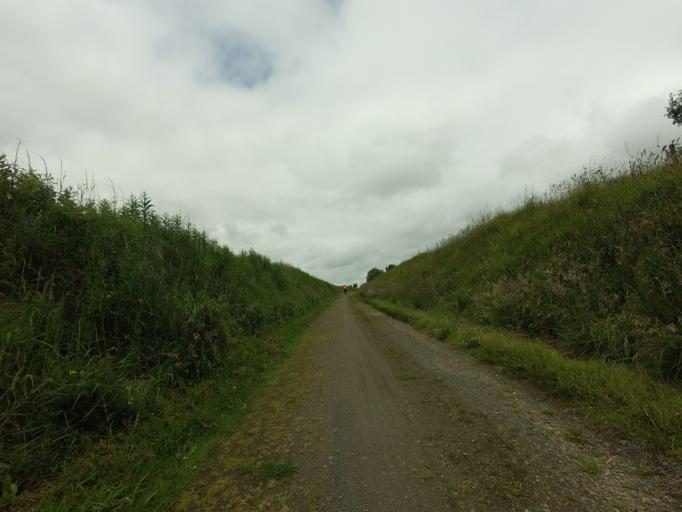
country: GB
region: Scotland
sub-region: Aberdeenshire
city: Mintlaw
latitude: 57.4987
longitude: -2.1409
